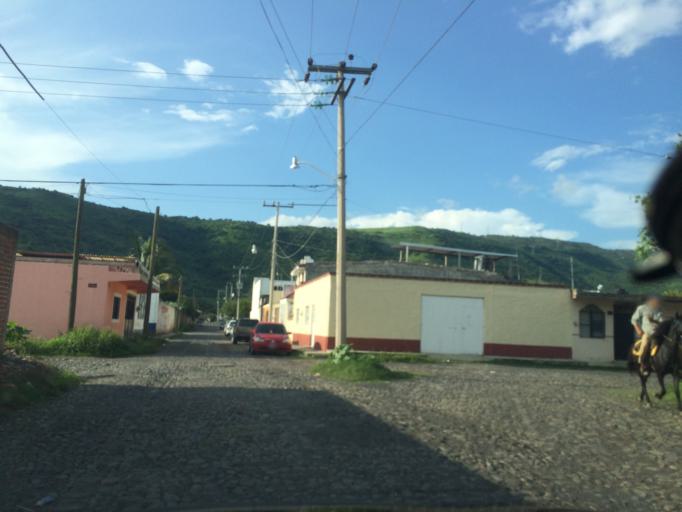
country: MX
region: Nayarit
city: Ixtlan del Rio
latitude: 21.0361
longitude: -104.3811
